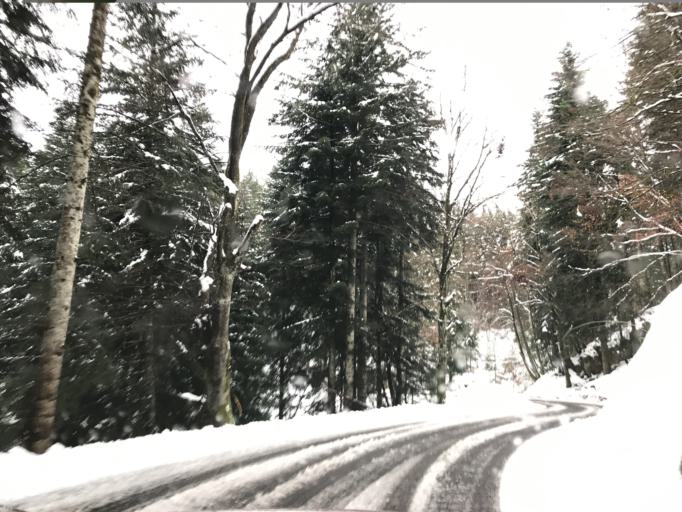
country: FR
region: Rhone-Alpes
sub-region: Departement de la Loire
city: Noiretable
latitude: 45.7495
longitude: 3.6715
